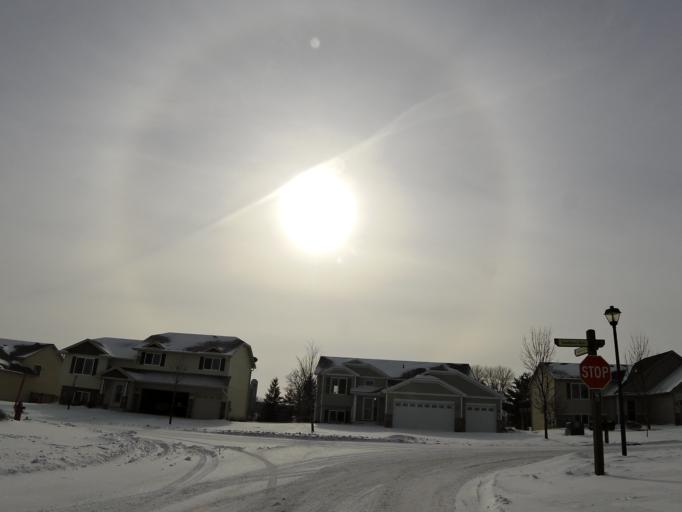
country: US
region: Minnesota
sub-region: Carver County
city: Mayer
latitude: 44.8920
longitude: -93.8741
